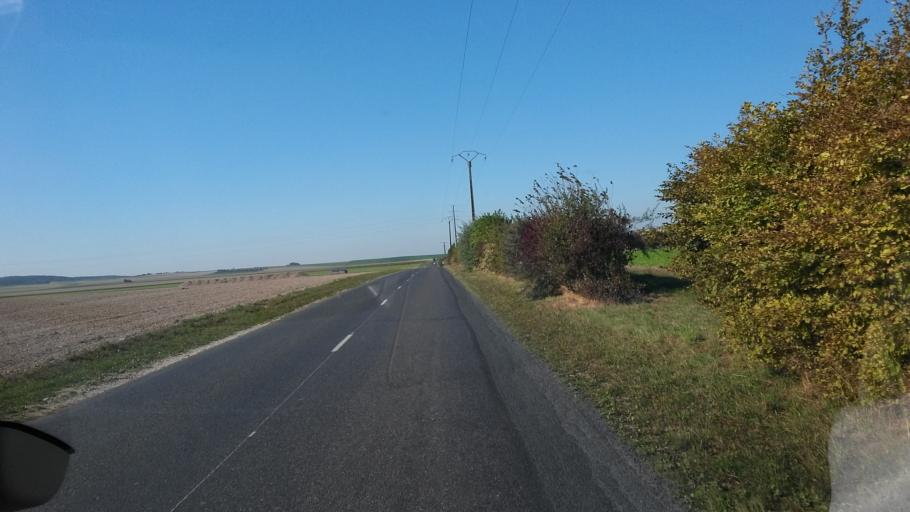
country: FR
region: Champagne-Ardenne
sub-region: Departement de la Marne
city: Connantre
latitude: 48.7371
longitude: 3.9005
